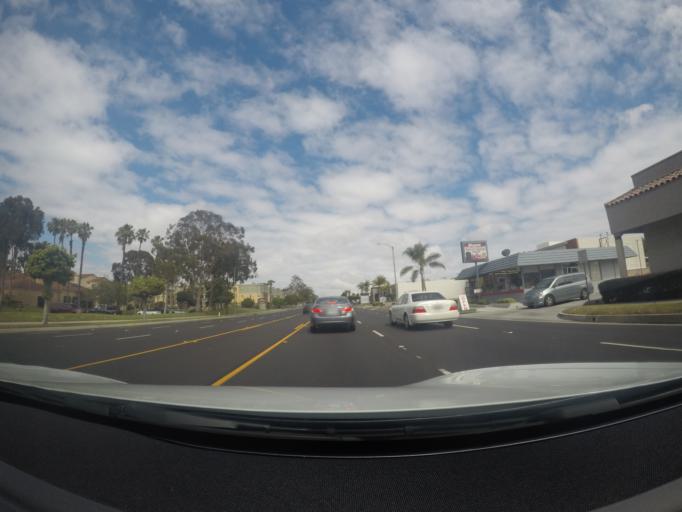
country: US
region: California
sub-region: Los Angeles County
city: Torrance
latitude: 33.8228
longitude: -118.3332
